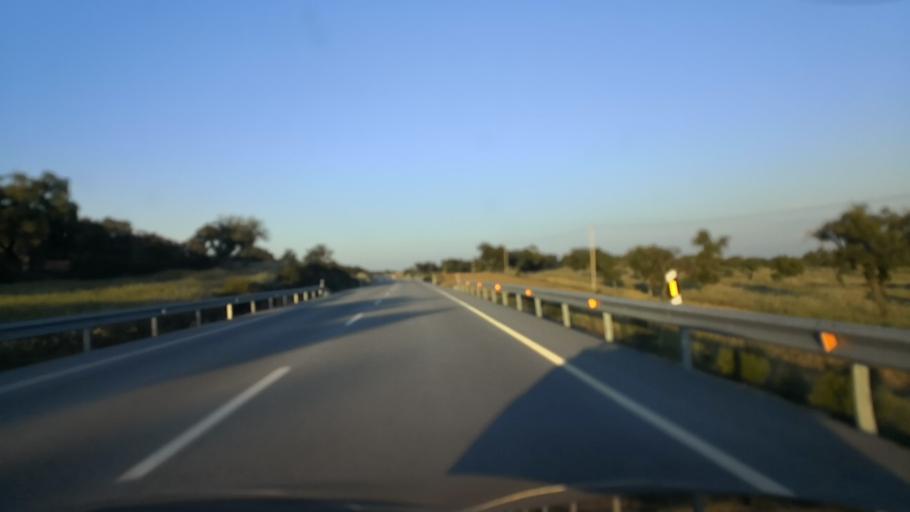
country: ES
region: Extremadura
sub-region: Provincia de Caceres
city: Carbajo
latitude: 39.5071
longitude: -7.1286
